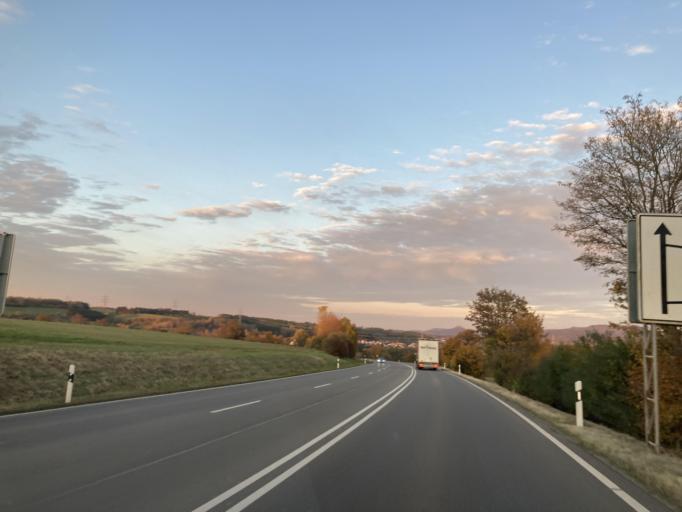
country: DE
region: Baden-Wuerttemberg
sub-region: Tuebingen Region
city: Dotternhausen
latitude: 48.2445
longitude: 8.8091
